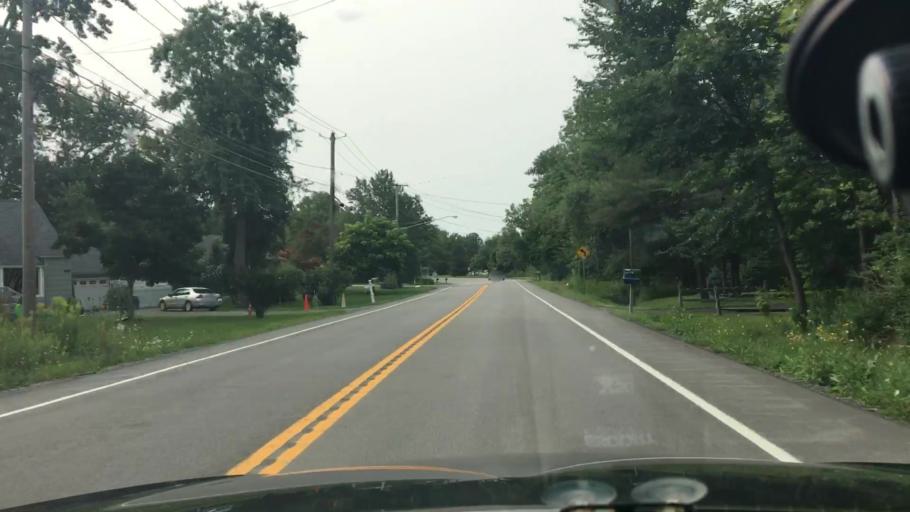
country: US
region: New York
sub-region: Erie County
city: Orchard Park
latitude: 42.7465
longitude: -78.7437
